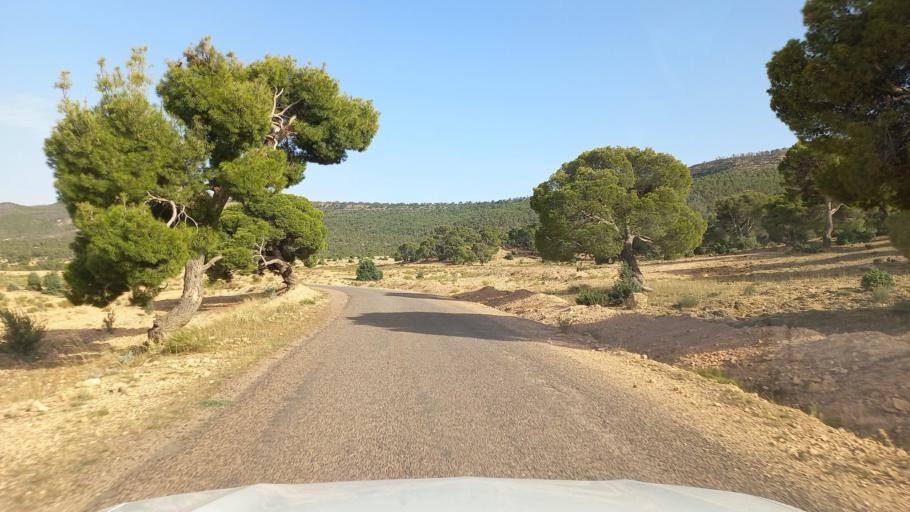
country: TN
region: Al Qasrayn
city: Kasserine
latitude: 35.3330
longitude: 8.8428
